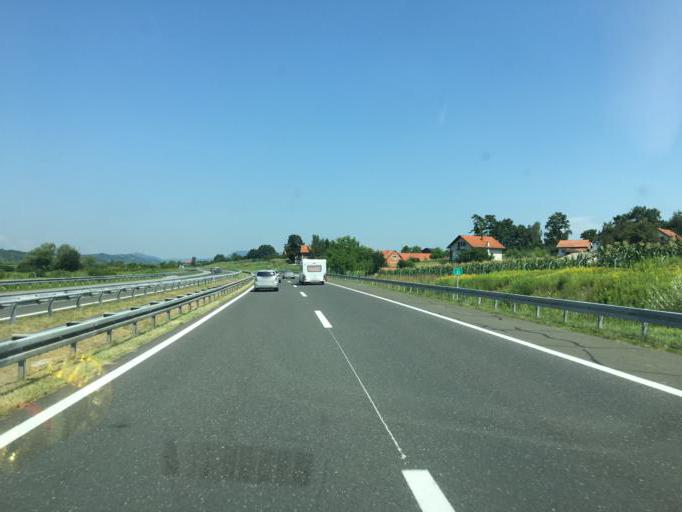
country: HR
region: Krapinsko-Zagorska
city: Zabok
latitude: 46.0413
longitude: 15.9264
